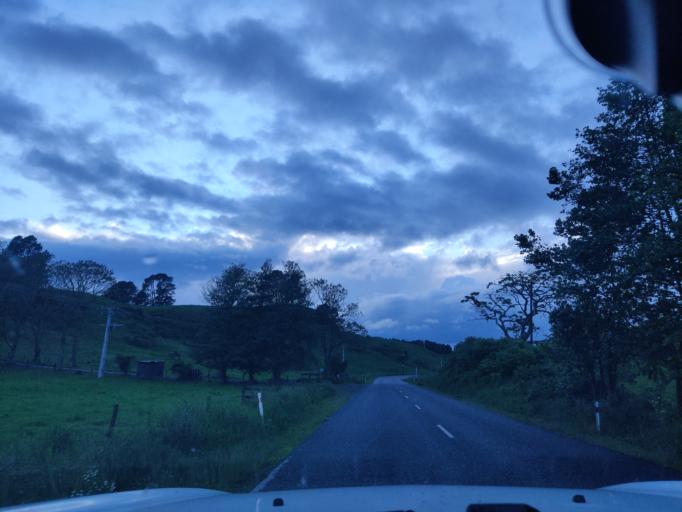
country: NZ
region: Waikato
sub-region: South Waikato District
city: Tokoroa
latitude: -38.1959
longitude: 175.8034
